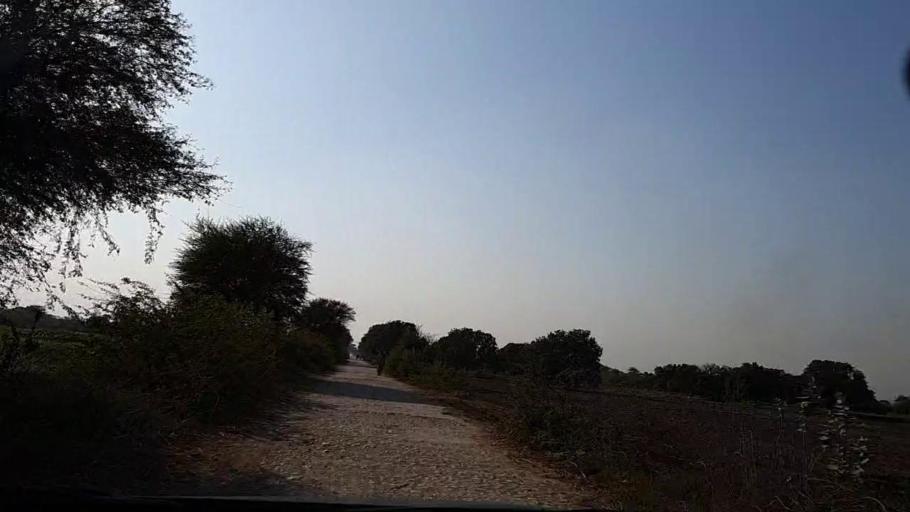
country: PK
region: Sindh
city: Tando Ghulam Ali
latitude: 25.2240
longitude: 68.9533
